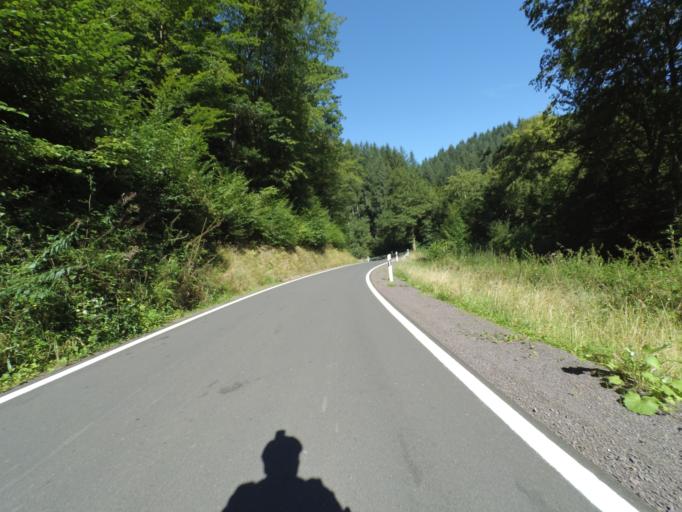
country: DE
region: Rheinland-Pfalz
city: Plein
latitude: 50.0350
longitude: 6.8763
